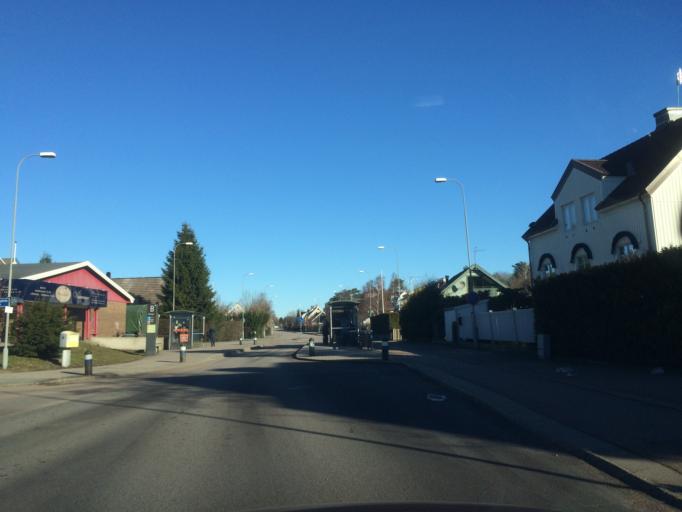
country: SE
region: Vaestra Goetaland
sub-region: Goteborg
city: Majorna
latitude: 57.6695
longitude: 11.8974
